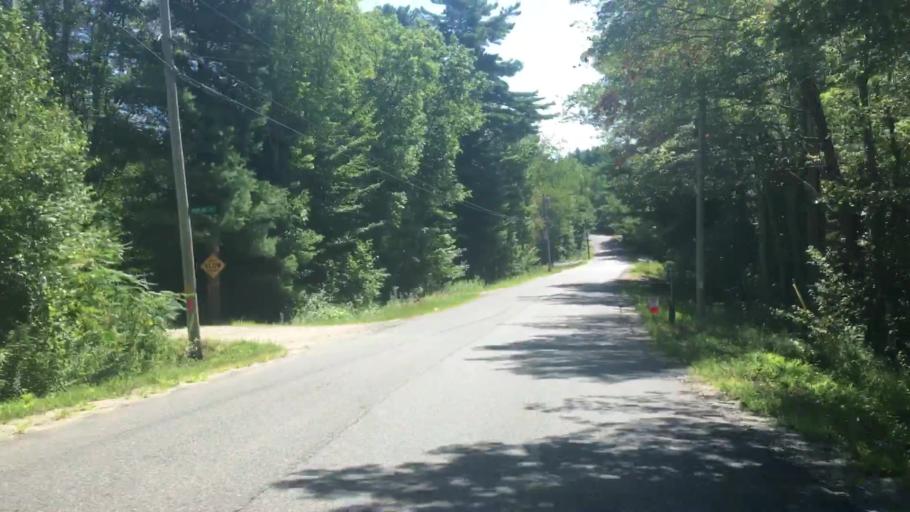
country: US
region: Maine
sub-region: Androscoggin County
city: Sabattus
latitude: 44.1213
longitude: -70.0330
